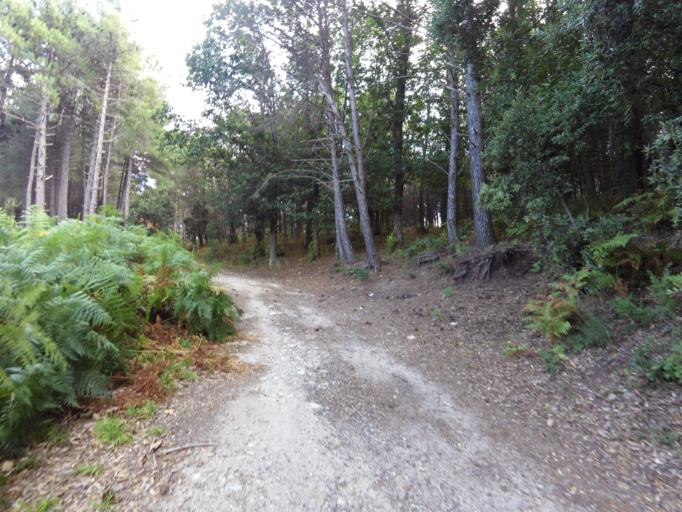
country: IT
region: Calabria
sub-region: Provincia di Reggio Calabria
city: Pazzano
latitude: 38.4757
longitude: 16.4061
